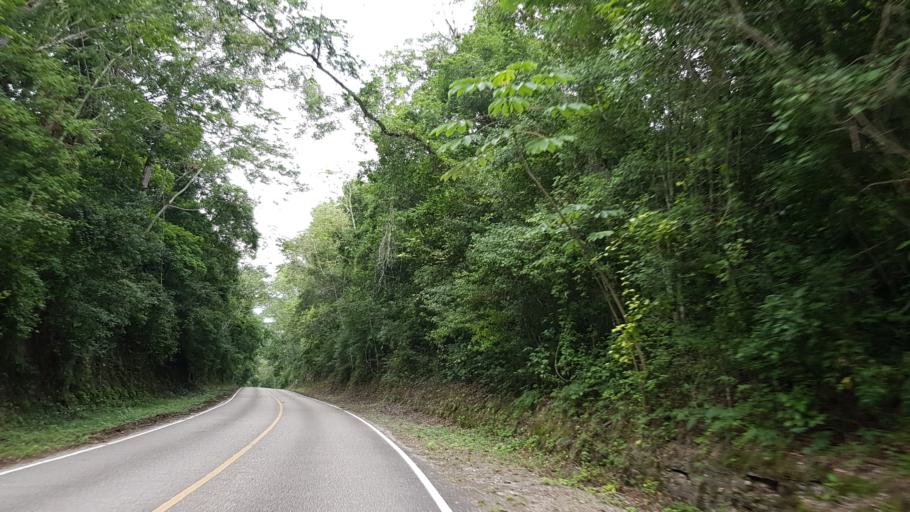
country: GT
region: Peten
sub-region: Municipio de San Jose
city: San Jose
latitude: 17.2148
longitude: -89.6120
